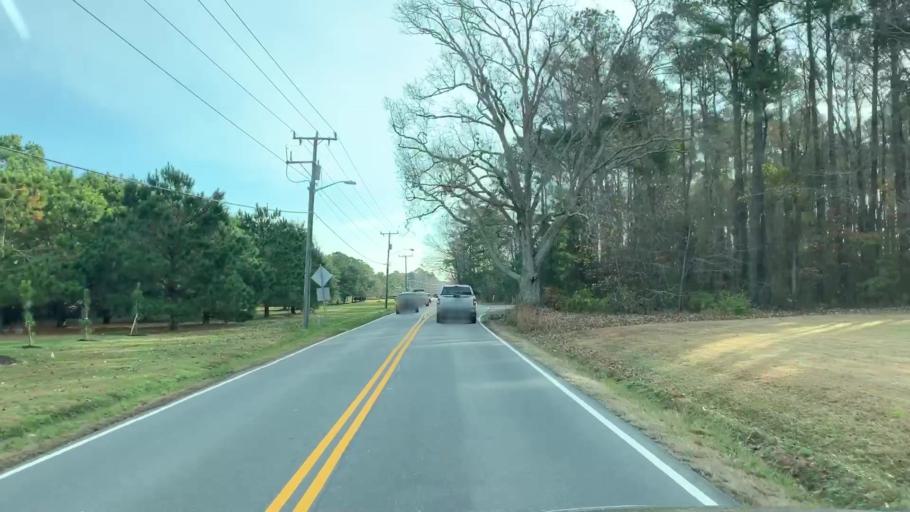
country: US
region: Virginia
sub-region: City of Virginia Beach
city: Virginia Beach
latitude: 36.7233
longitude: -76.0634
